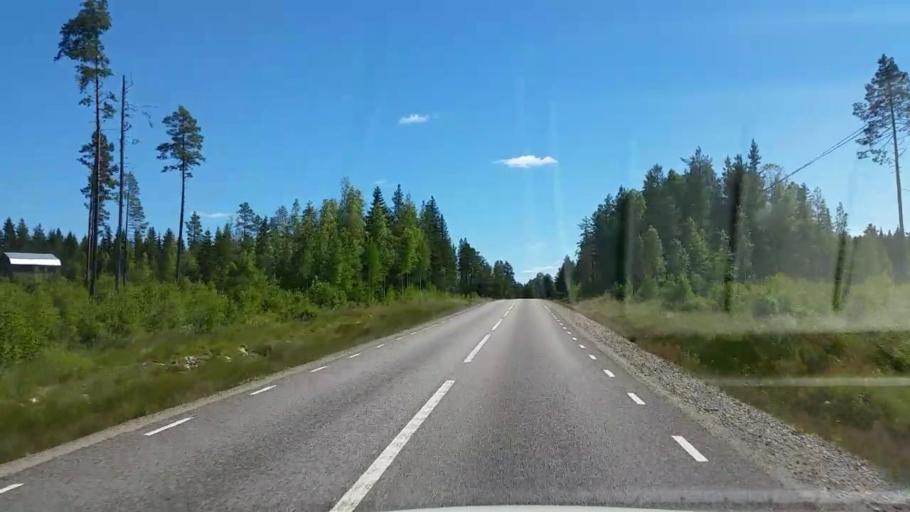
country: SE
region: Gaevleborg
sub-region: Ovanakers Kommun
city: Edsbyn
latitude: 61.4572
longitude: 15.7029
